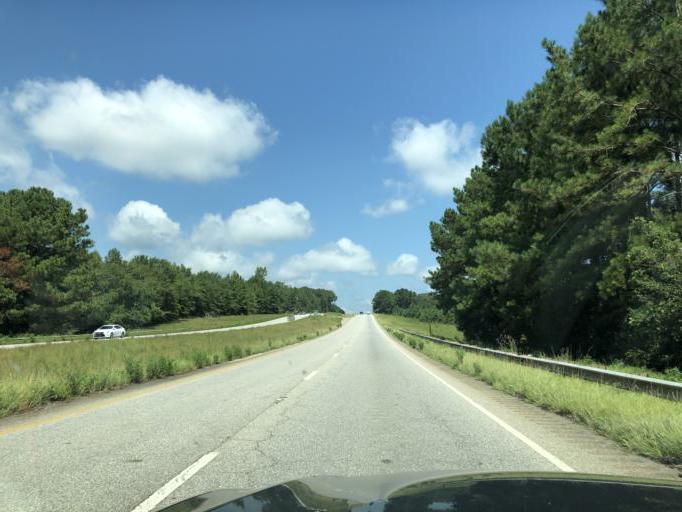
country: US
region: Alabama
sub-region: Henry County
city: Abbeville
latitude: 31.6284
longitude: -85.2786
